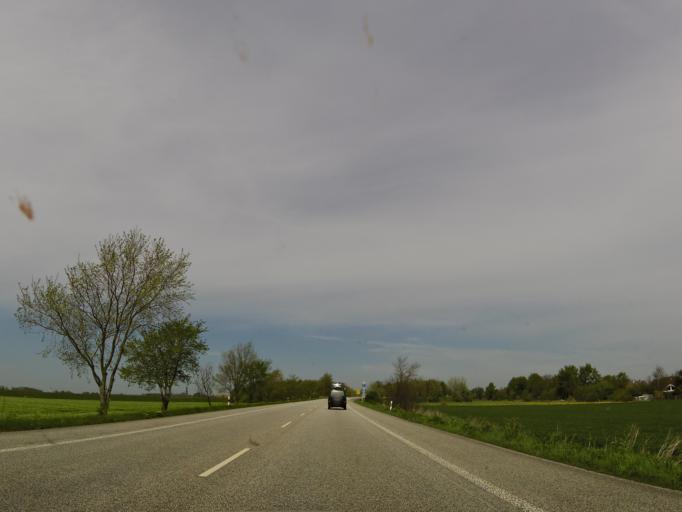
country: DE
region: Schleswig-Holstein
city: Karolinenkoog
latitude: 54.3045
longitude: 8.9619
